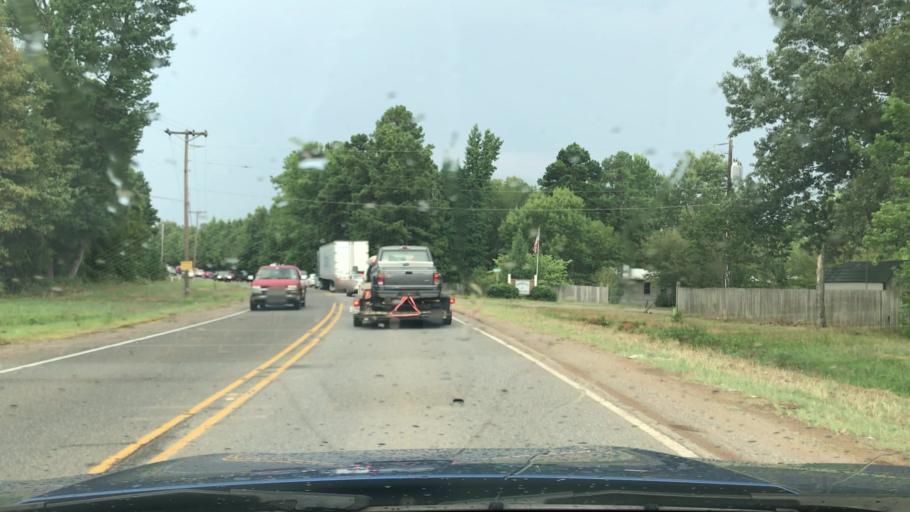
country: US
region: Louisiana
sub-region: Caddo Parish
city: Greenwood
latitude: 32.4486
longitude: -94.0100
